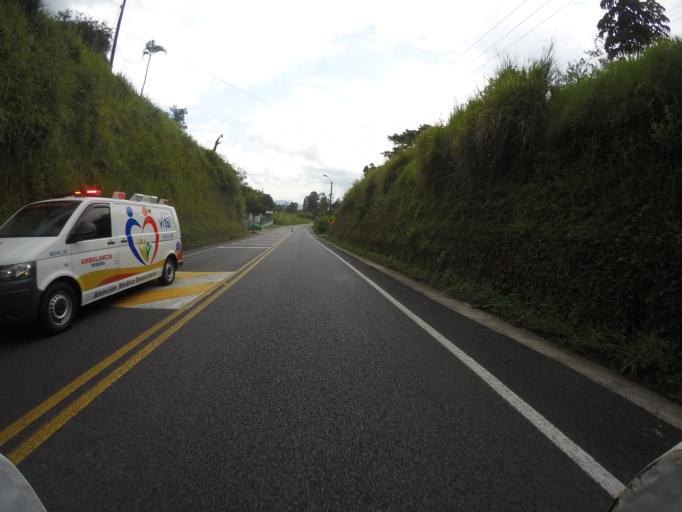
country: CO
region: Risaralda
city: Pereira
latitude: 4.7700
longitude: -75.6906
